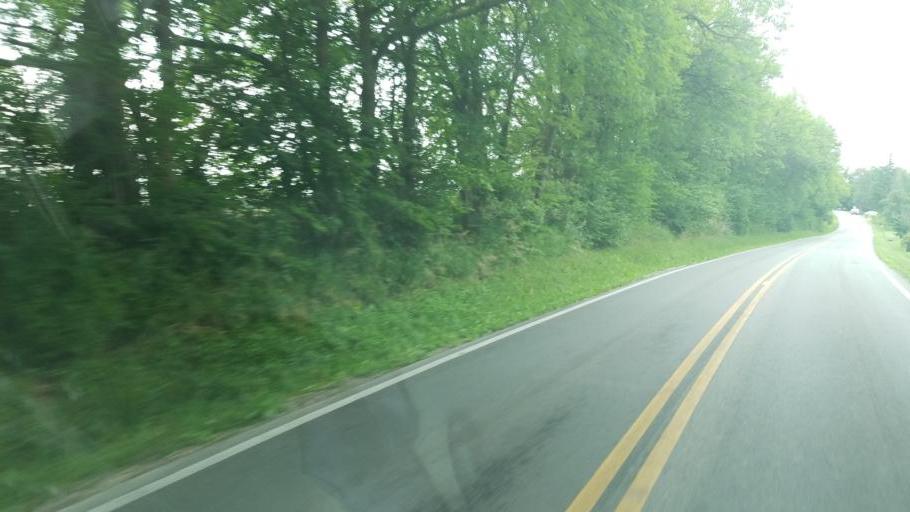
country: US
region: Ohio
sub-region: Delaware County
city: Ashley
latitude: 40.3963
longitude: -82.9476
